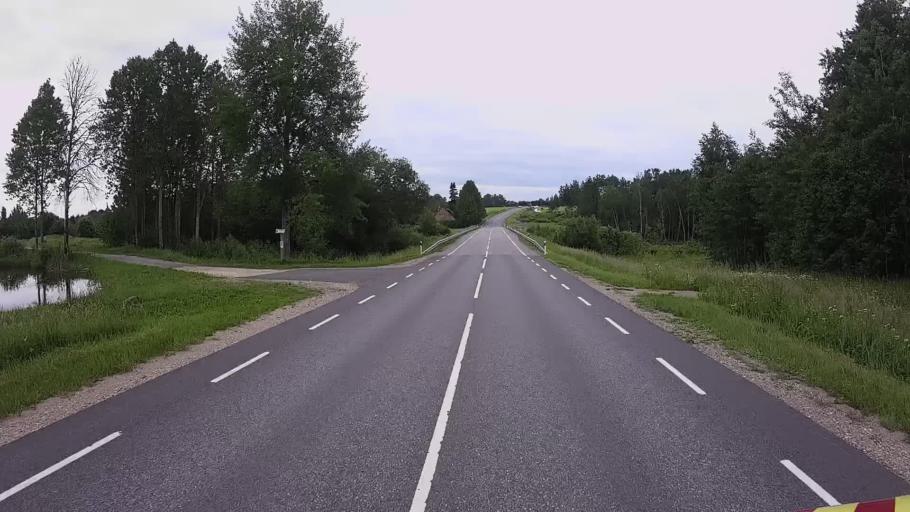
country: EE
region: Viljandimaa
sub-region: Karksi vald
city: Karksi-Nuia
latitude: 58.1485
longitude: 25.5942
